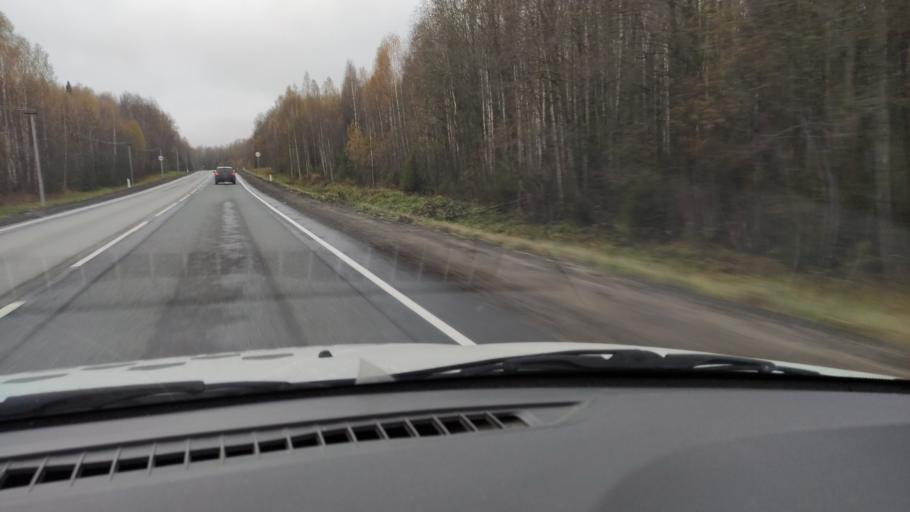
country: RU
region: Kirov
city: Belaya Kholunitsa
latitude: 58.9202
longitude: 51.1225
